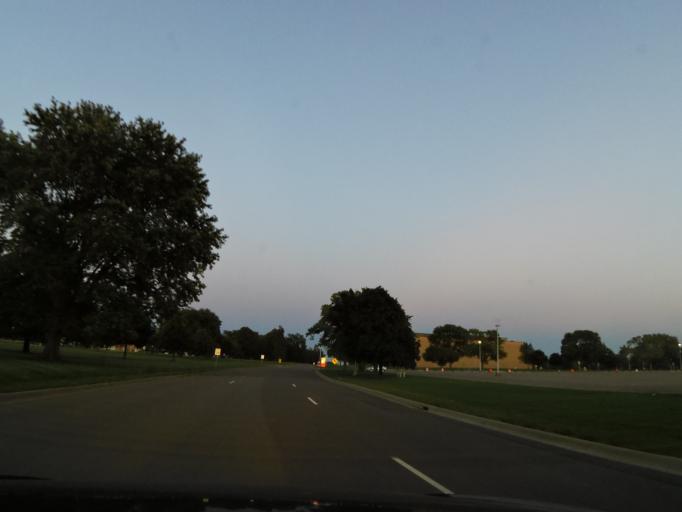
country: US
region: Minnesota
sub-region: Ramsey County
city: Maplewood
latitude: 44.9532
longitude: -92.9930
